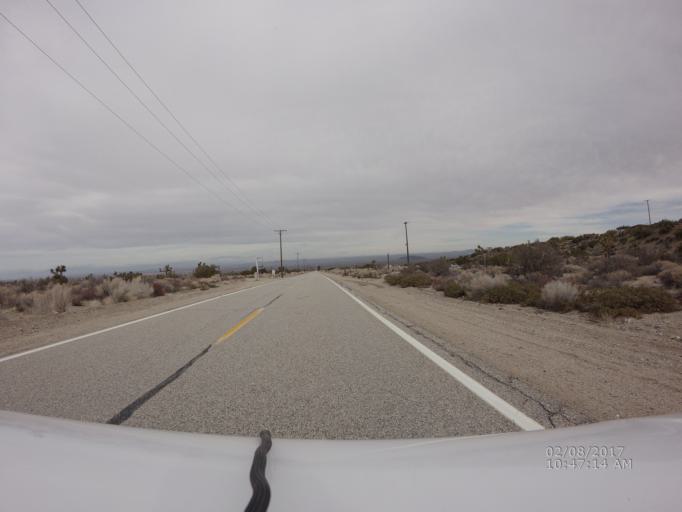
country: US
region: California
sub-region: San Bernardino County
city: Pinon Hills
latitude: 34.4544
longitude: -117.7649
